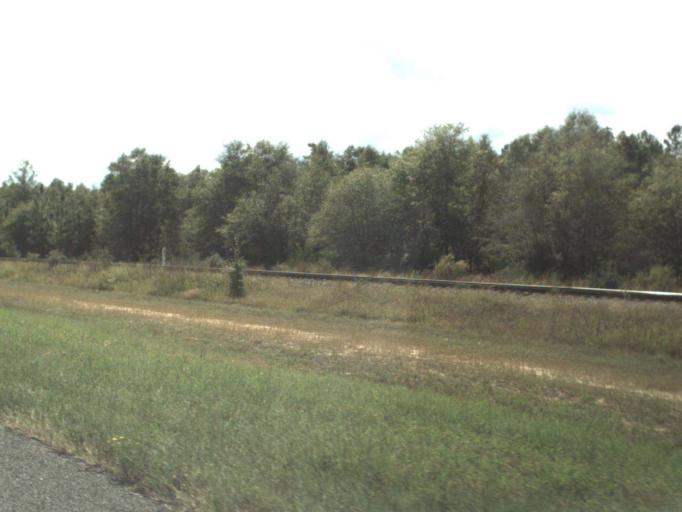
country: US
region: Florida
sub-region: Washington County
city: Chipley
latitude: 30.6024
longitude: -85.3974
